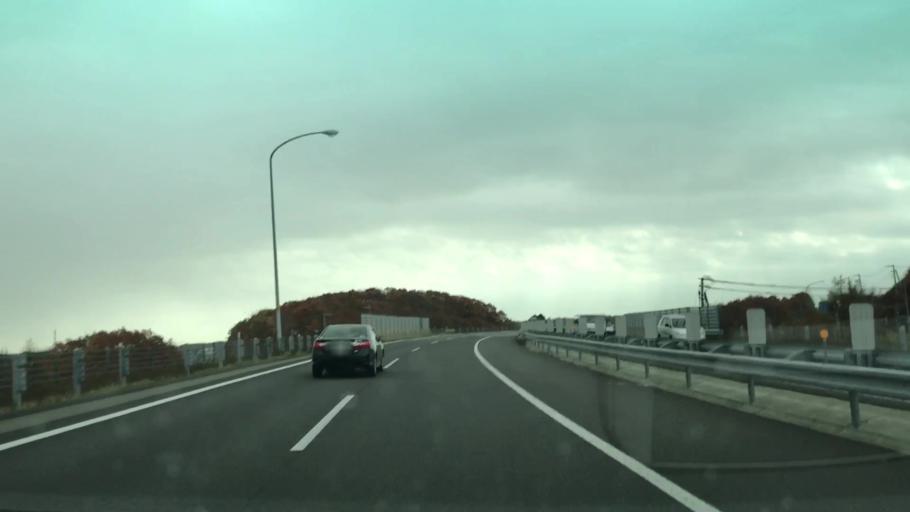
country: JP
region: Hokkaido
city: Tomakomai
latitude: 42.6547
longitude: 141.8299
